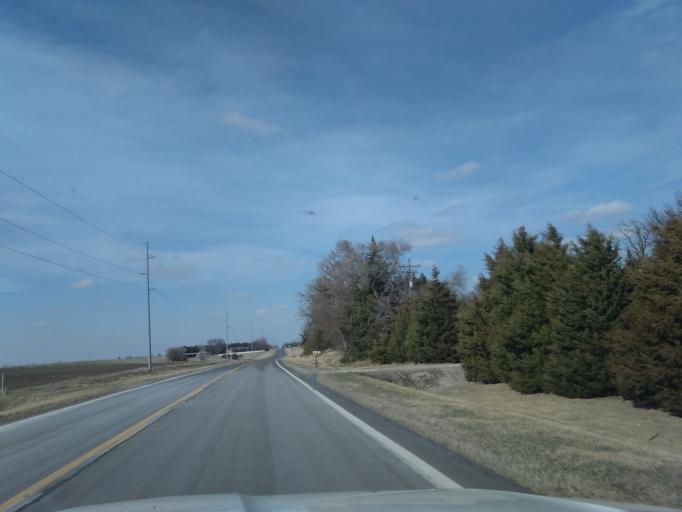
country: US
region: Nebraska
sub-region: Gage County
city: Beatrice
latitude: 40.2014
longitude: -96.9353
